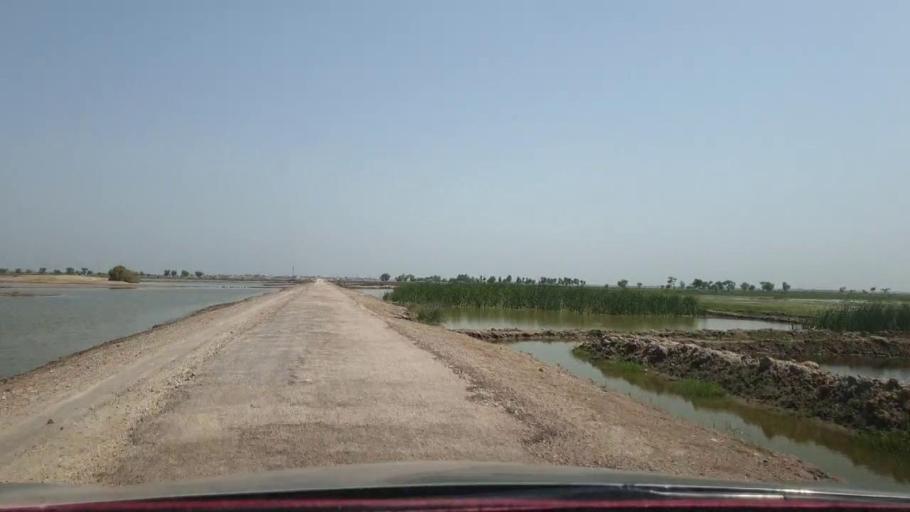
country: PK
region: Sindh
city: Warah
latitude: 27.3775
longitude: 67.7899
